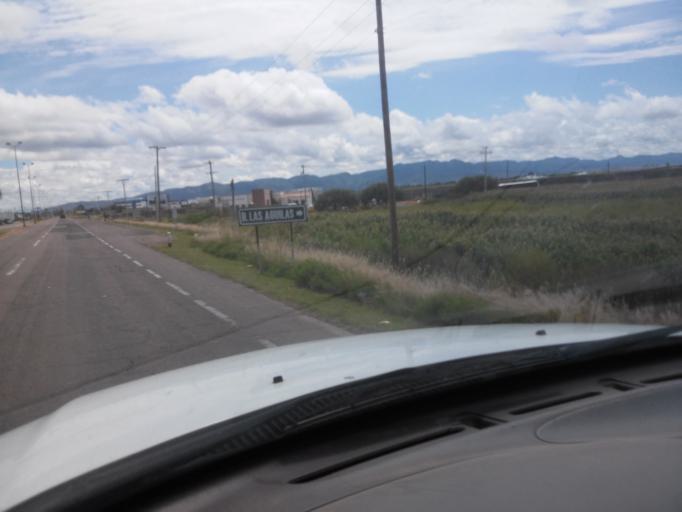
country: MX
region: Durango
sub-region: Durango
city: Jose Refugio Salcido
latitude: 24.0234
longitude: -104.5467
